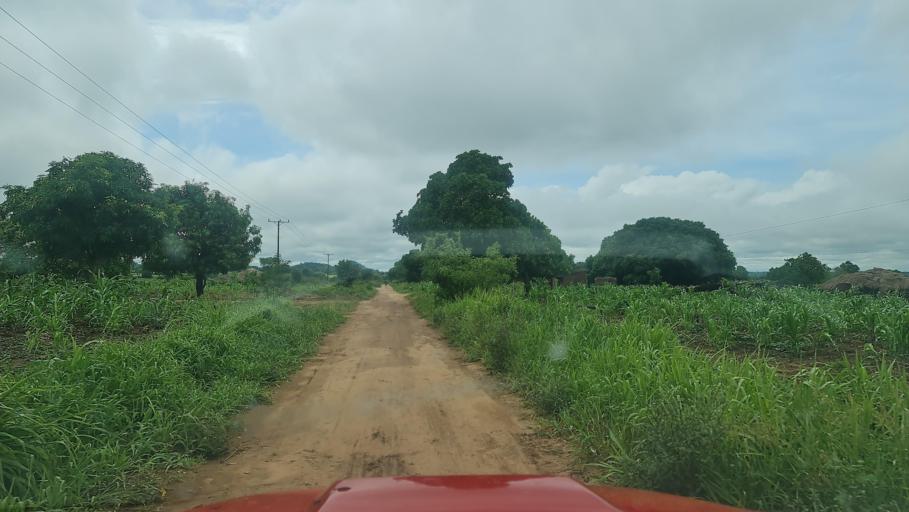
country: MW
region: Southern Region
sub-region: Nsanje District
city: Nsanje
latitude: -17.1826
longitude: 35.9137
